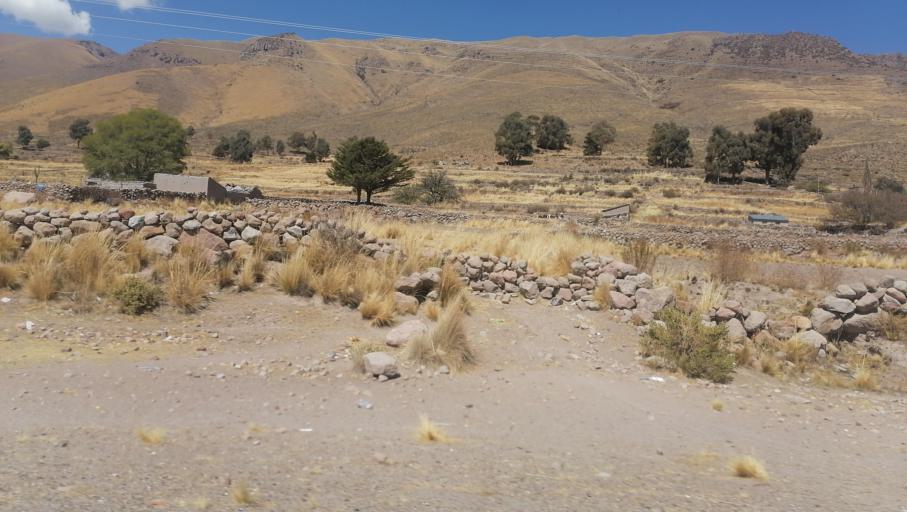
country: BO
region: Oruro
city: Challapata
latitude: -18.9912
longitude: -66.7785
